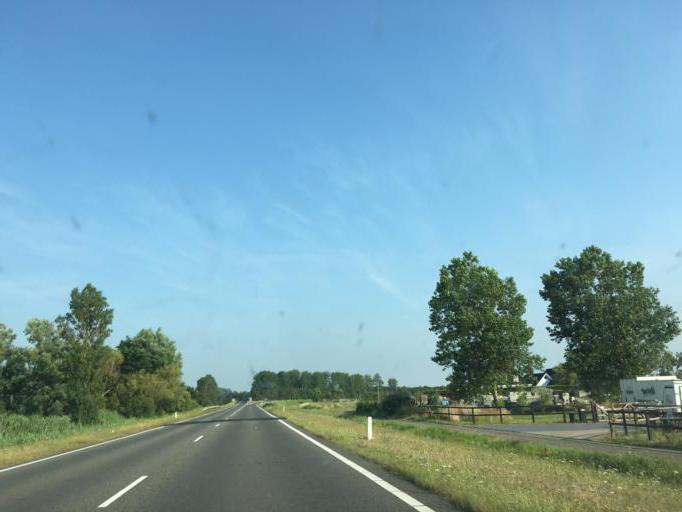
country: NL
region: South Holland
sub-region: Gemeente Noordwijk
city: Noordwijk-Binnen
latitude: 52.2255
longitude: 4.4485
